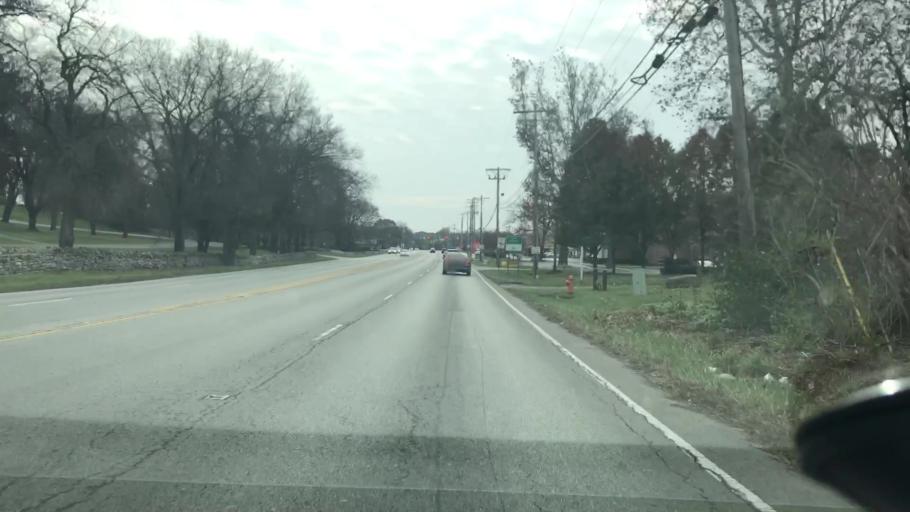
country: US
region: Ohio
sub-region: Franklin County
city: Upper Arlington
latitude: 40.0016
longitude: -83.0781
